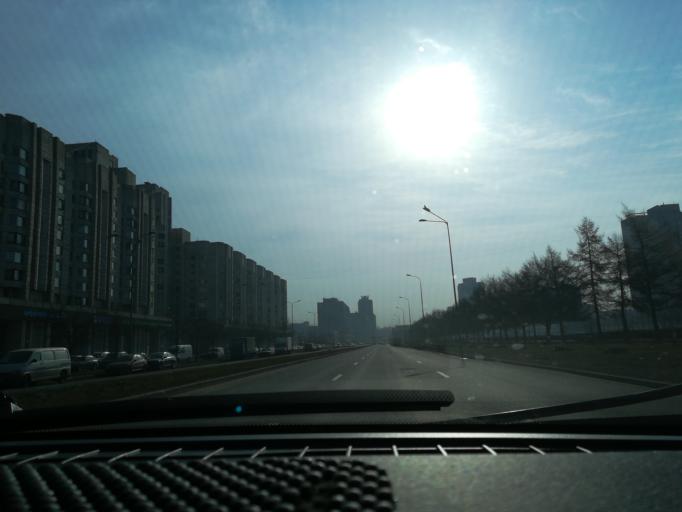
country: RU
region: St.-Petersburg
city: Vasyl'evsky Ostrov
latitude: 59.9494
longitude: 30.2252
